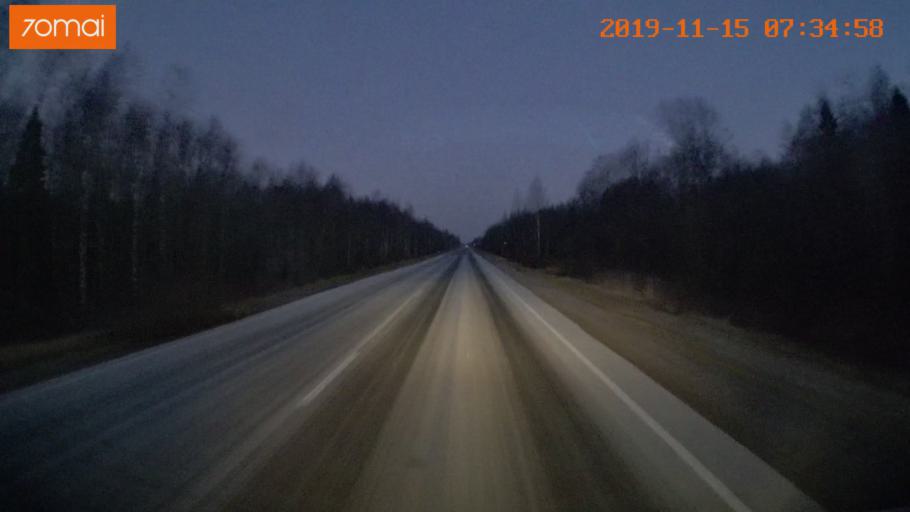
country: RU
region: Vologda
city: Sheksna
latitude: 58.7262
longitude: 38.4593
